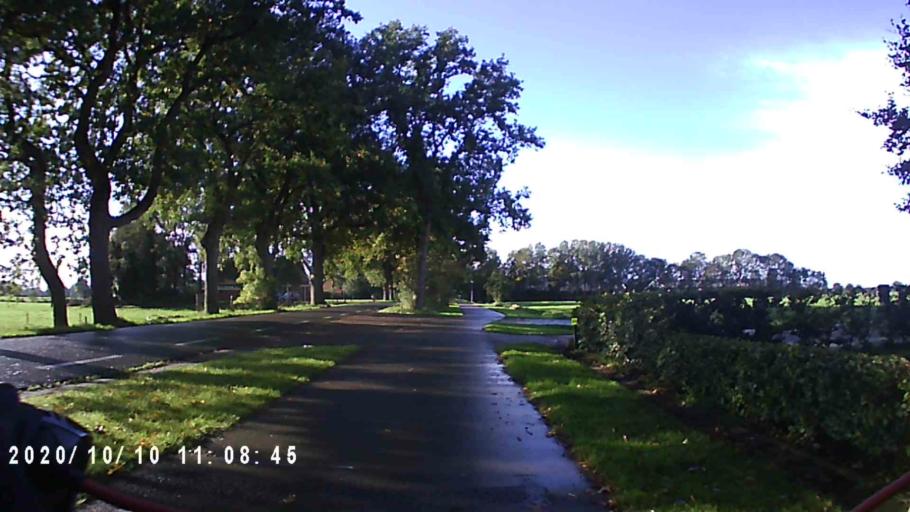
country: NL
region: Friesland
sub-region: Gemeente Smallingerland
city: Drachtstercompagnie
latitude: 53.1202
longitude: 6.2100
